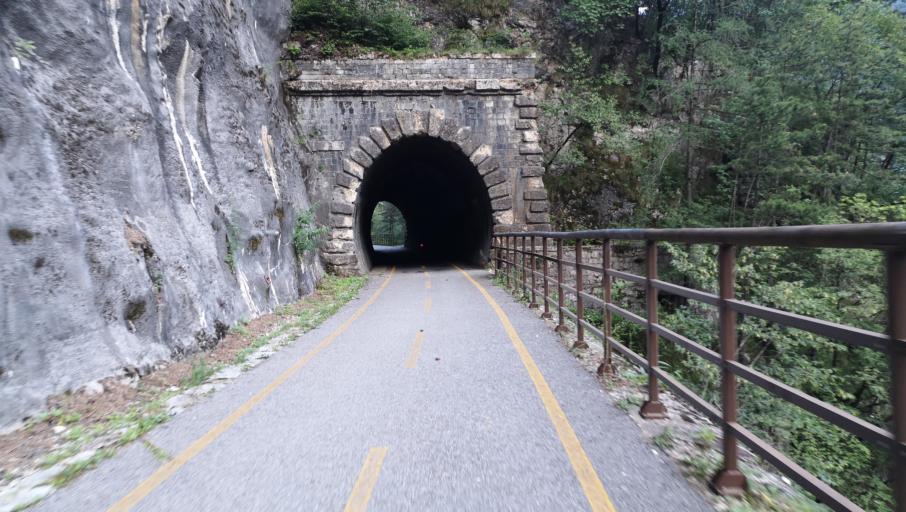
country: IT
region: Friuli Venezia Giulia
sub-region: Provincia di Udine
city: Dogna
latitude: 46.4619
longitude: 13.2972
